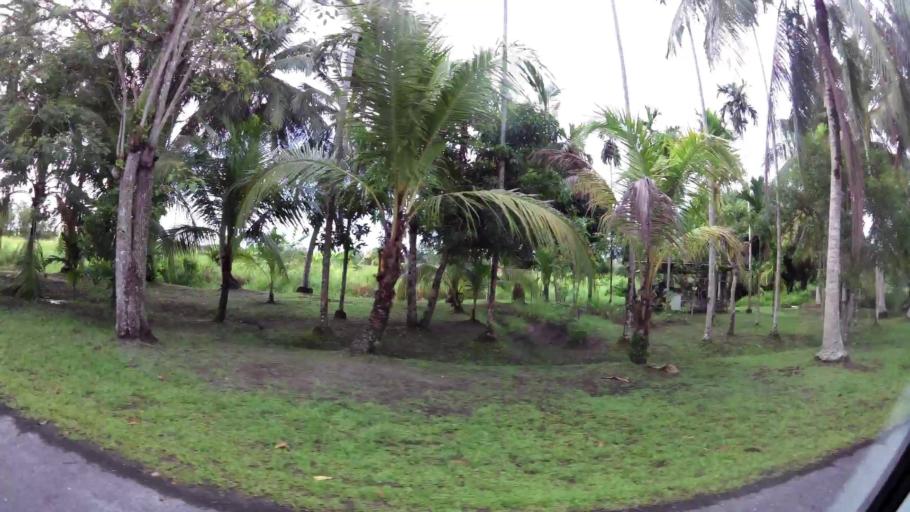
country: BN
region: Belait
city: Seria
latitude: 4.5960
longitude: 114.3269
